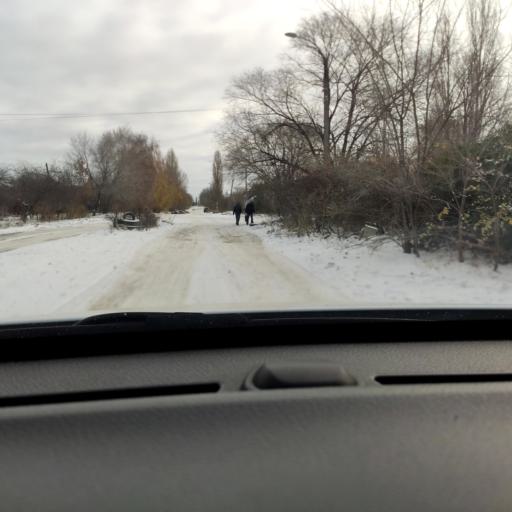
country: RU
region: Voronezj
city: Maslovka
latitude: 51.6311
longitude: 39.2768
